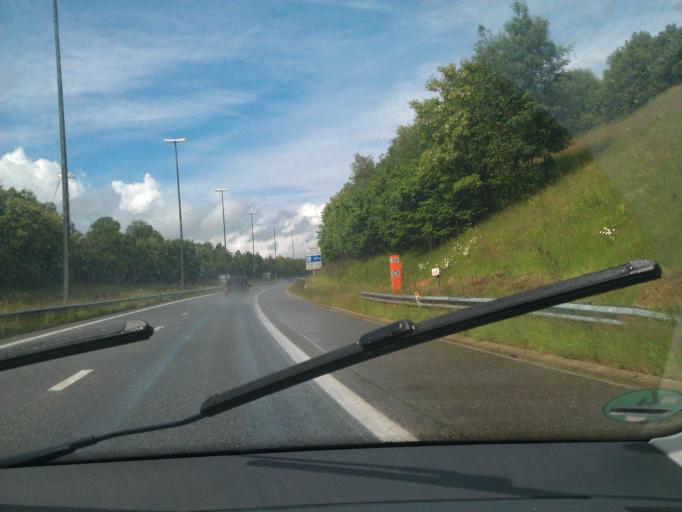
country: BE
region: Wallonia
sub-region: Province de Liege
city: Saint-Vith
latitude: 50.3048
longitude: 6.0790
